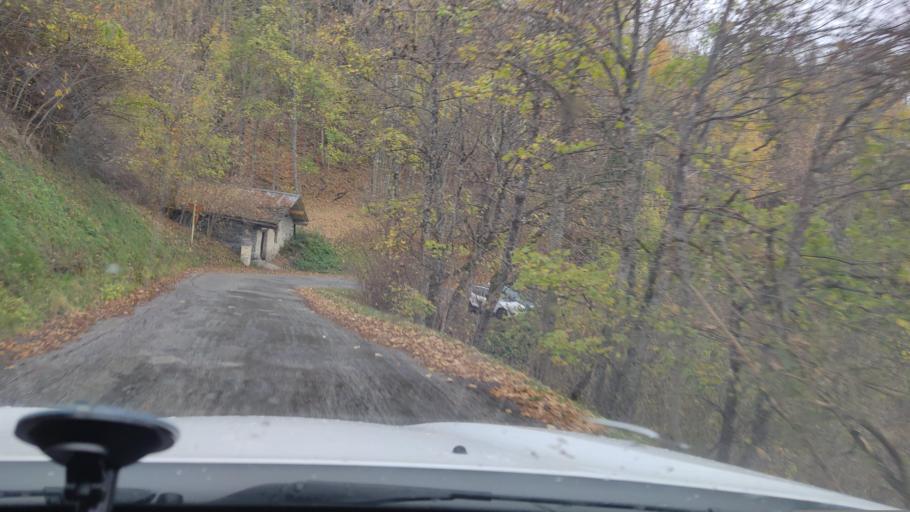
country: FR
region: Rhone-Alpes
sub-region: Departement de la Savoie
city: Bourg-Saint-Maurice
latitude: 45.5989
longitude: 6.7764
